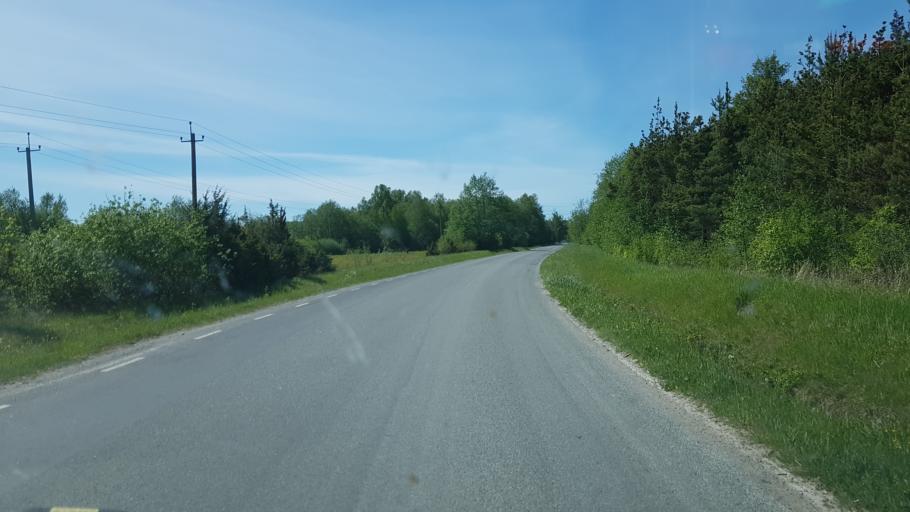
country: EE
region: Saare
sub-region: Kuressaare linn
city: Kuressaare
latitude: 58.2765
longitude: 22.5006
